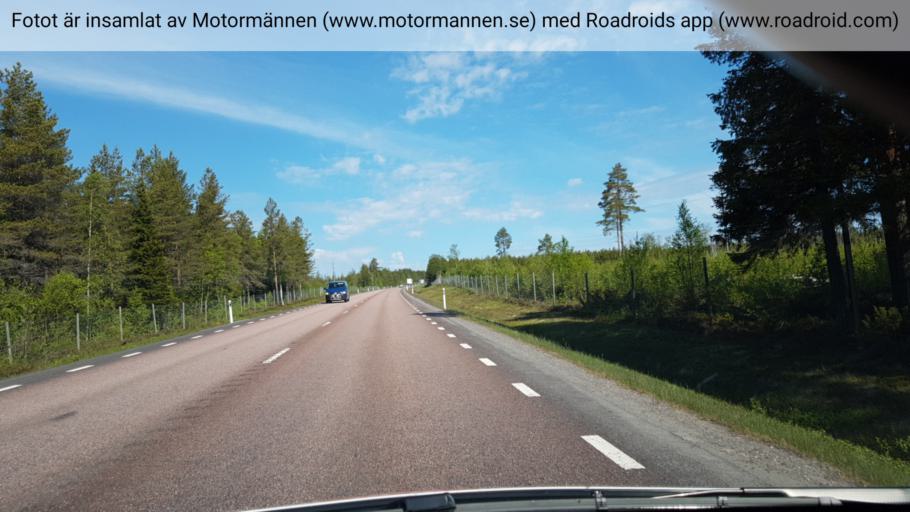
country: SE
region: Vaesterbotten
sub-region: Skelleftea Kommun
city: Burea
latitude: 64.4155
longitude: 21.2906
